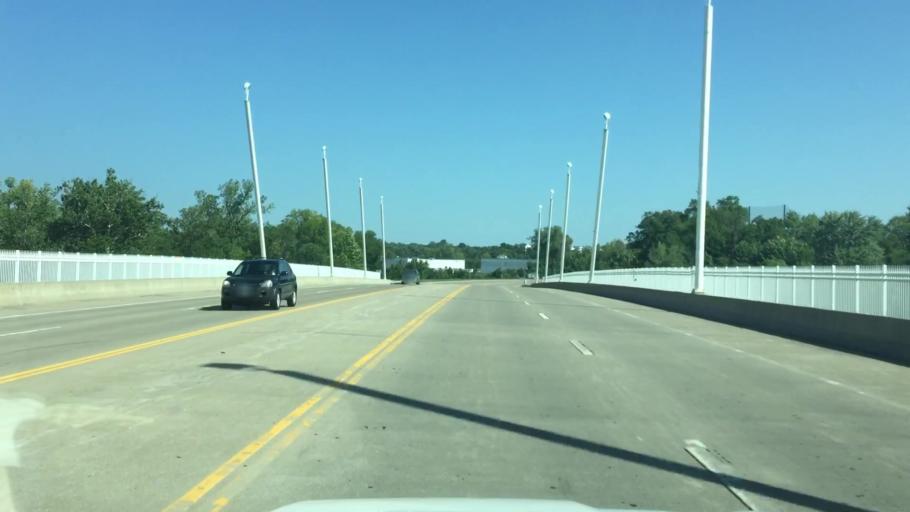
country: US
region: Missouri
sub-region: Jefferson County
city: Arnold
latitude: 38.4565
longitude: -90.3606
